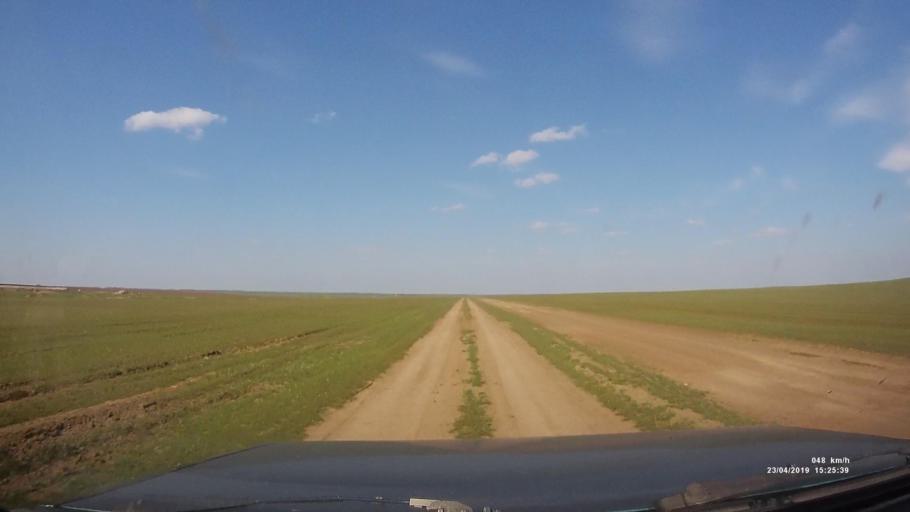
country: RU
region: Rostov
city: Remontnoye
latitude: 46.5423
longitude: 42.9831
